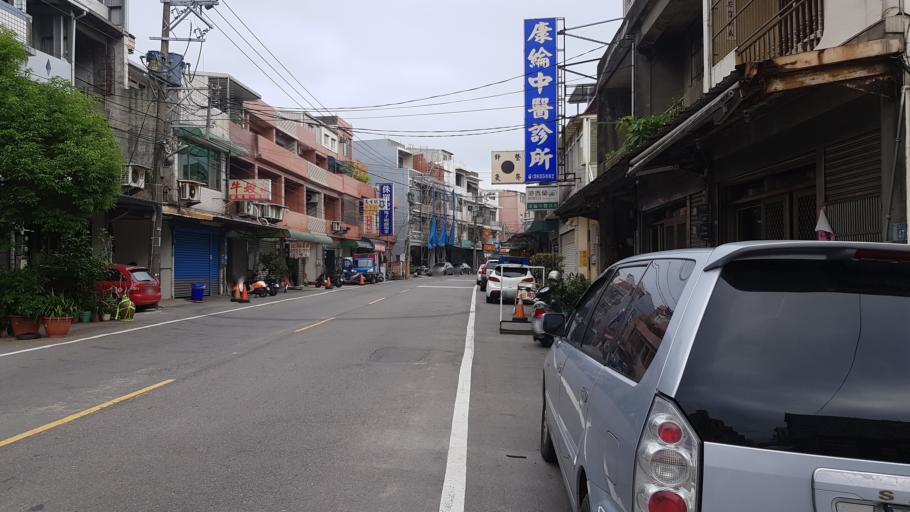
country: TW
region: Taiwan
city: Taoyuan City
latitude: 25.0789
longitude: 121.2571
